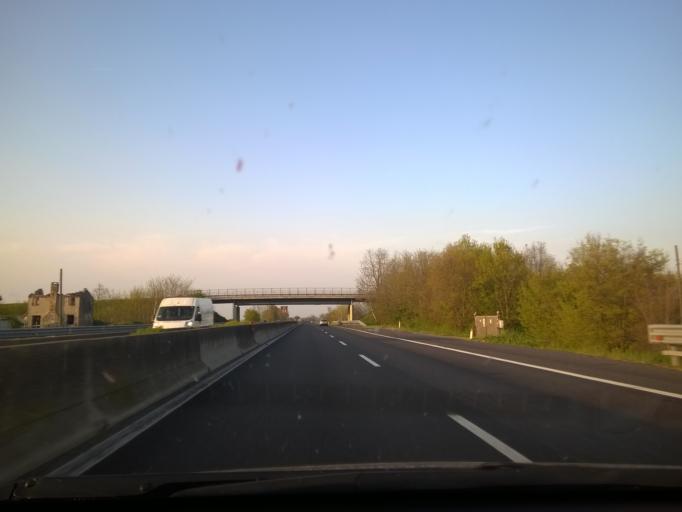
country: IT
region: Veneto
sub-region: Provincia di Rovigo
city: Fiesso Umbertiano
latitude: 44.9613
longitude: 11.6441
